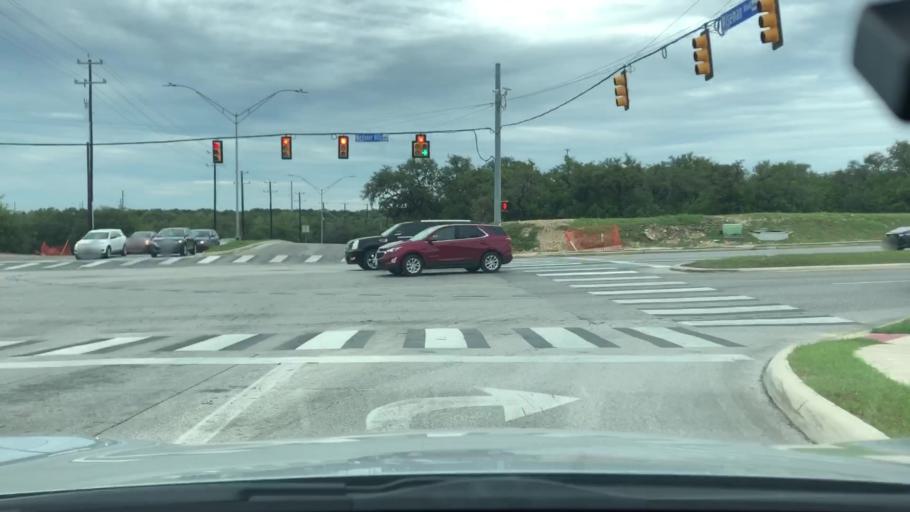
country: US
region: Texas
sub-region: Bexar County
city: Leon Valley
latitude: 29.4682
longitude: -98.6760
